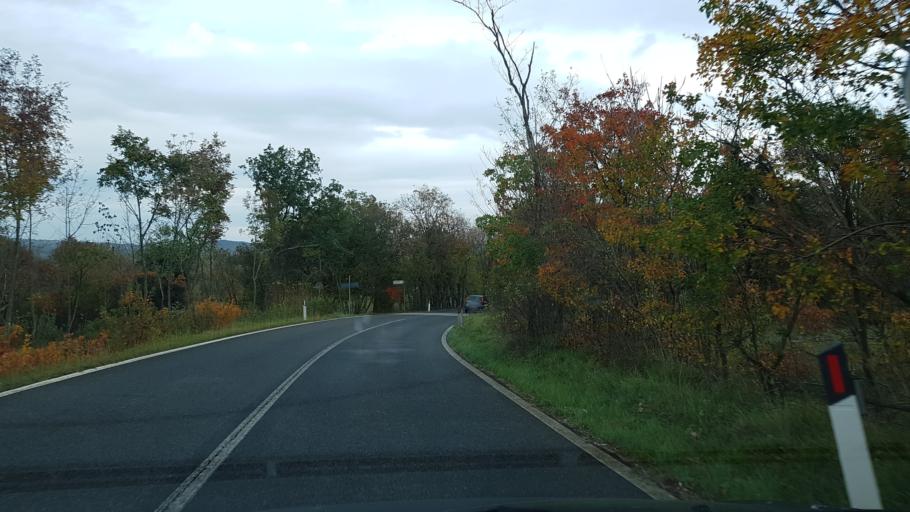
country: IT
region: Friuli Venezia Giulia
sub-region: Provincia di Gorizia
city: Doberdo del Lago
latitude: 45.8576
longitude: 13.5491
